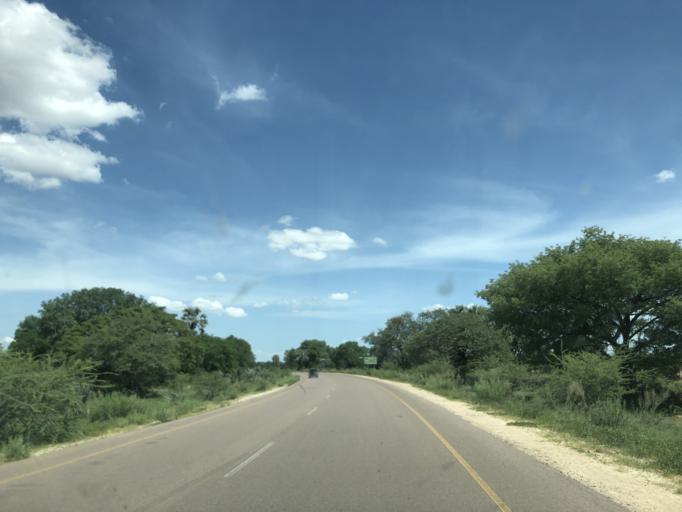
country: AO
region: Cunene
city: Ondjiva
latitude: -16.8884
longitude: 15.4928
